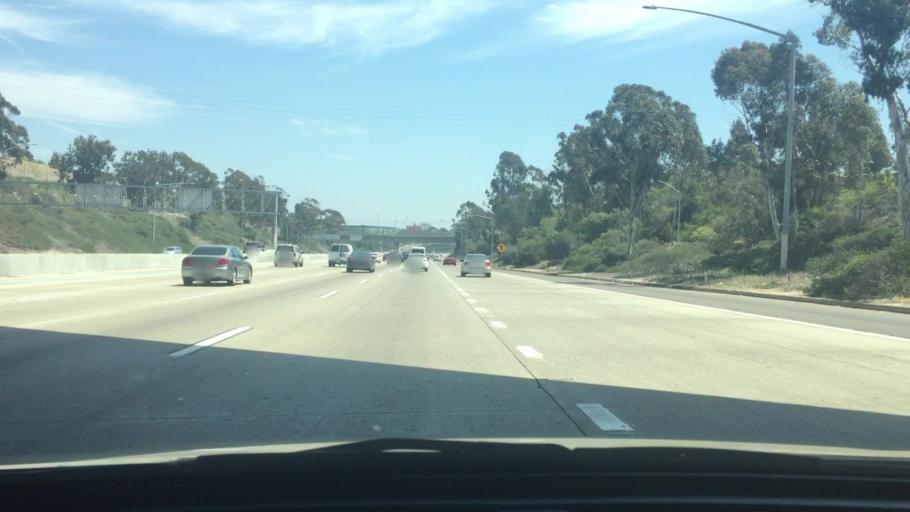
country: US
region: California
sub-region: San Diego County
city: National City
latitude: 32.7114
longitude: -117.1009
